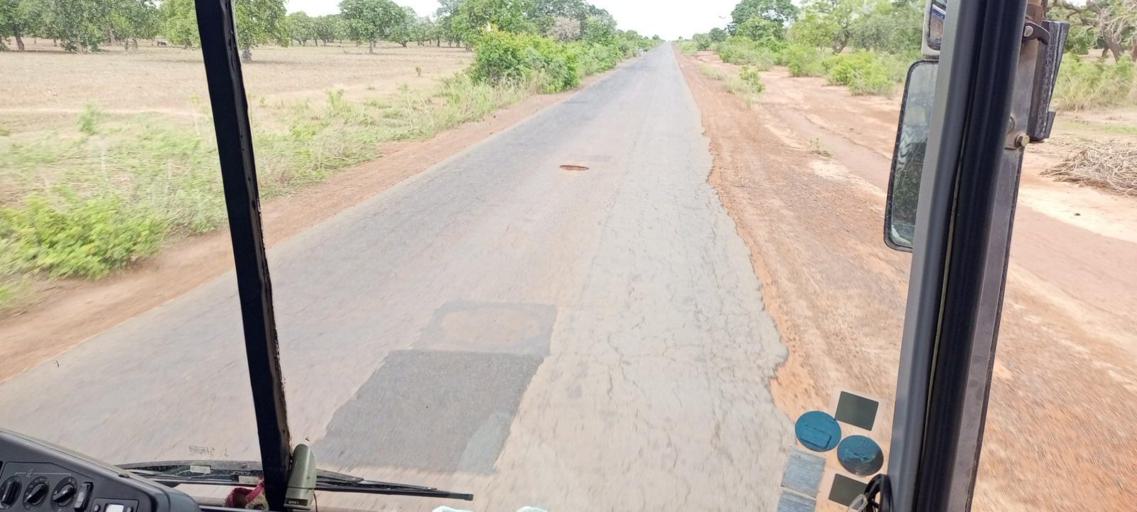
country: ML
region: Segou
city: Bla
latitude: 12.7272
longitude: -5.7253
